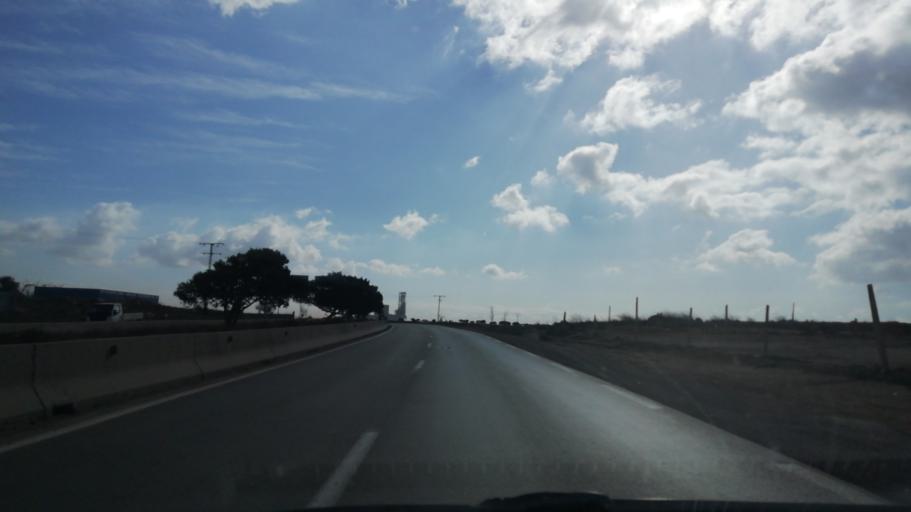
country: DZ
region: Oran
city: Ain el Bya
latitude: 35.7833
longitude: -0.2836
